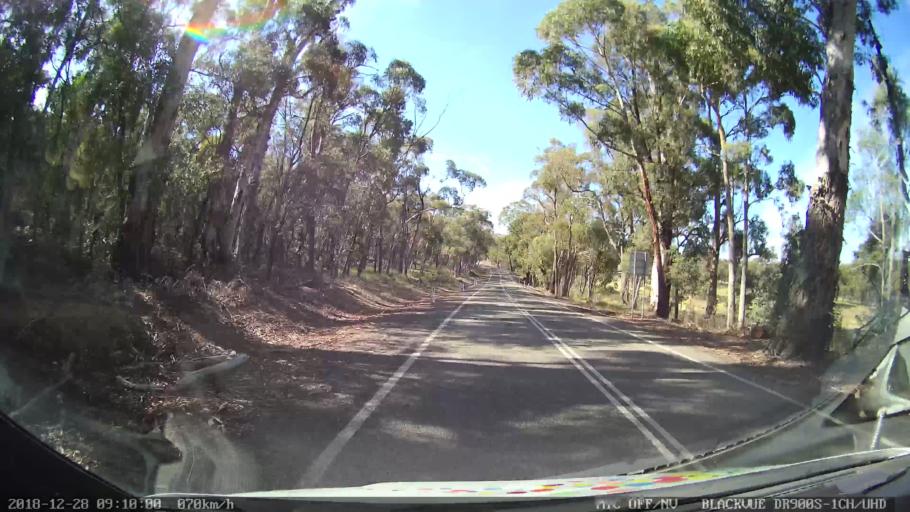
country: AU
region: New South Wales
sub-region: Upper Lachlan Shire
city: Crookwell
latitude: -34.2272
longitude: 149.3360
